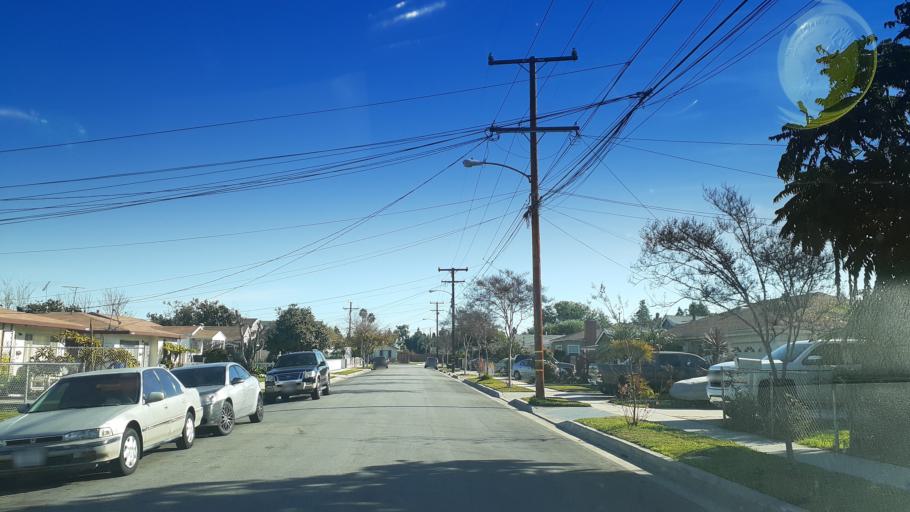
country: US
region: California
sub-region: Los Angeles County
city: Cerritos
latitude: 33.8549
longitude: -118.0705
